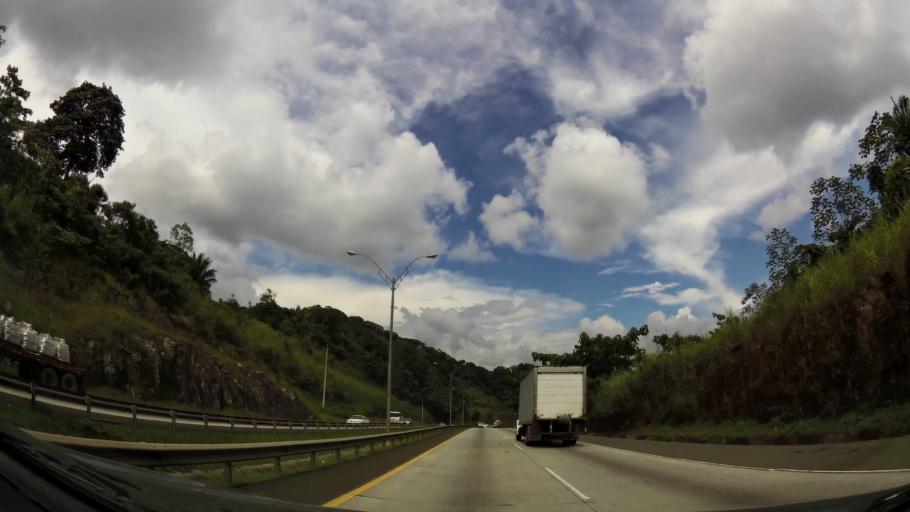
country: PA
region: Panama
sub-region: Distrito de Panama
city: Paraiso
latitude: 9.0061
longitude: -79.6488
